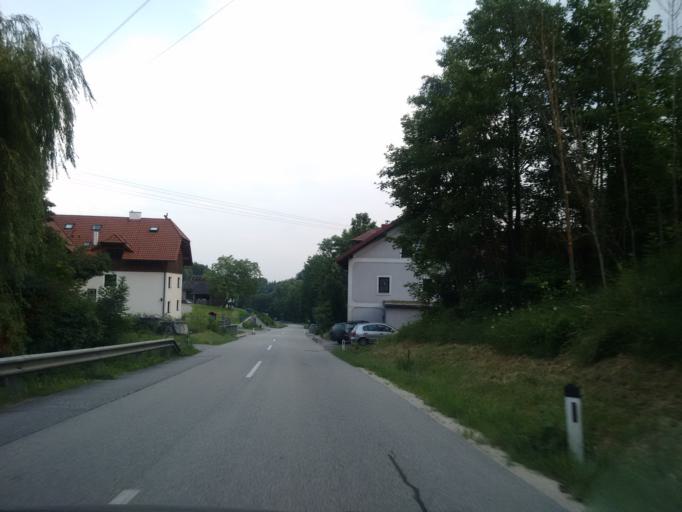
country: AT
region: Upper Austria
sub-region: Politischer Bezirk Urfahr-Umgebung
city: Altenberg bei Linz
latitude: 48.3531
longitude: 14.3319
